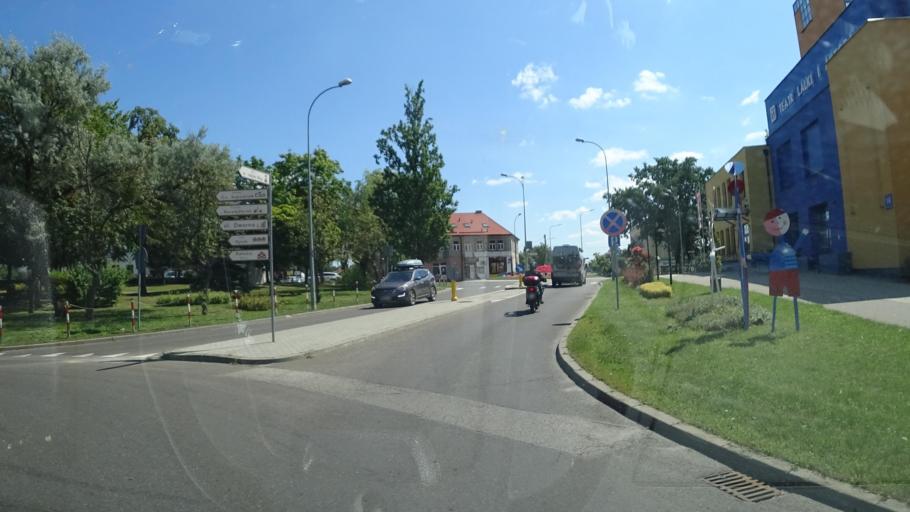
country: PL
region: Podlasie
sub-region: Lomza
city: Lomza
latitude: 53.1750
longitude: 22.0786
